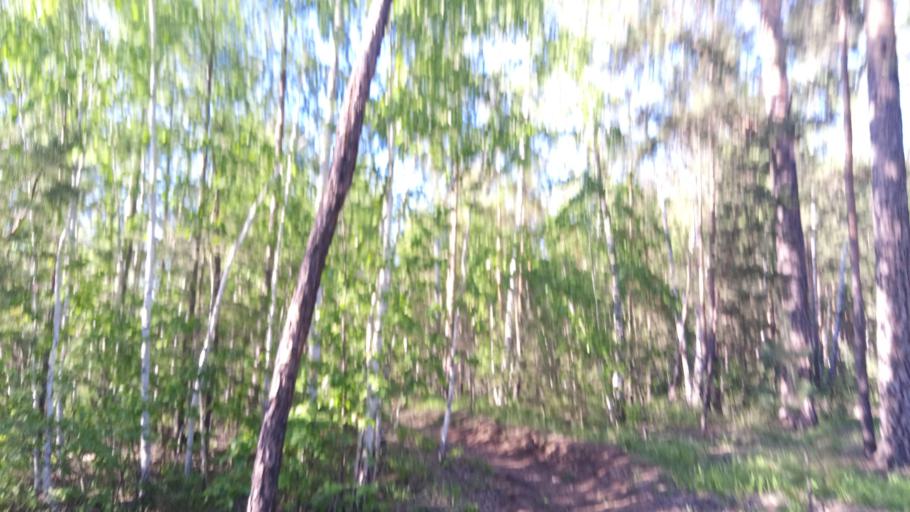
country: RU
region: Chelyabinsk
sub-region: Gorod Chelyabinsk
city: Chelyabinsk
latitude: 55.1249
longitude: 61.3437
